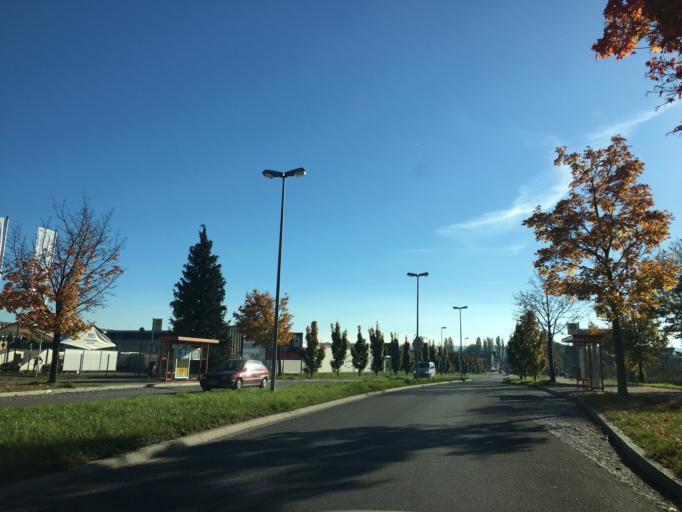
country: CH
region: Thurgau
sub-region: Kreuzlingen District
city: Gottlieben
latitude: 47.6803
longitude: 9.1469
